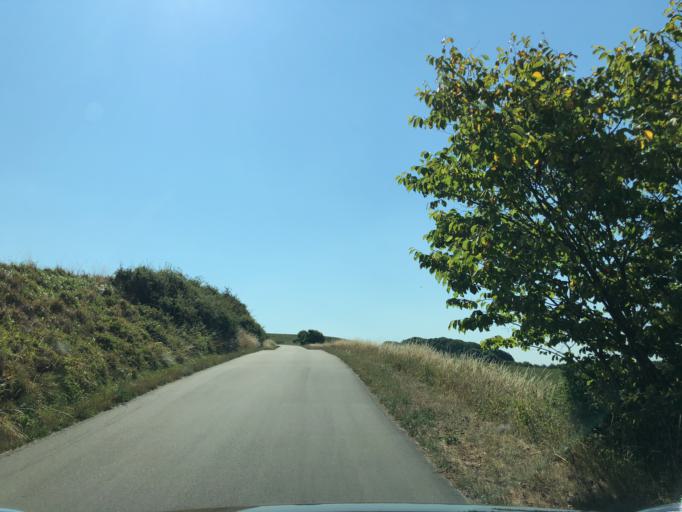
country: DK
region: Zealand
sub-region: Odsherred Kommune
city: Hojby
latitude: 55.9588
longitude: 11.4733
